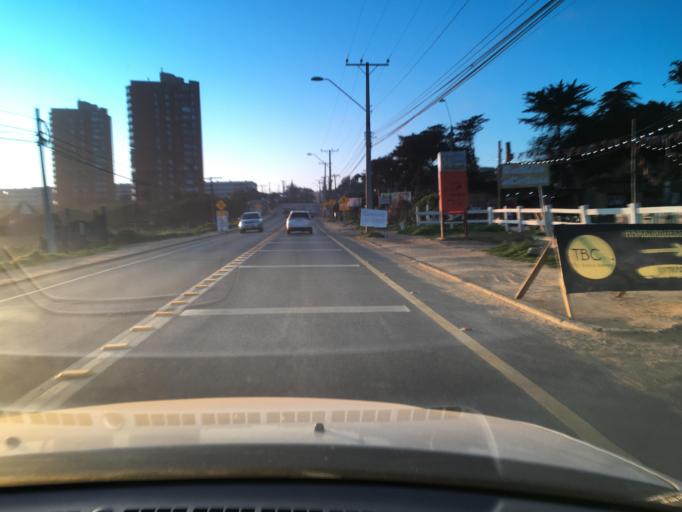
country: CL
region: Valparaiso
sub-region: San Antonio Province
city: El Tabo
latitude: -33.4507
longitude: -71.6748
